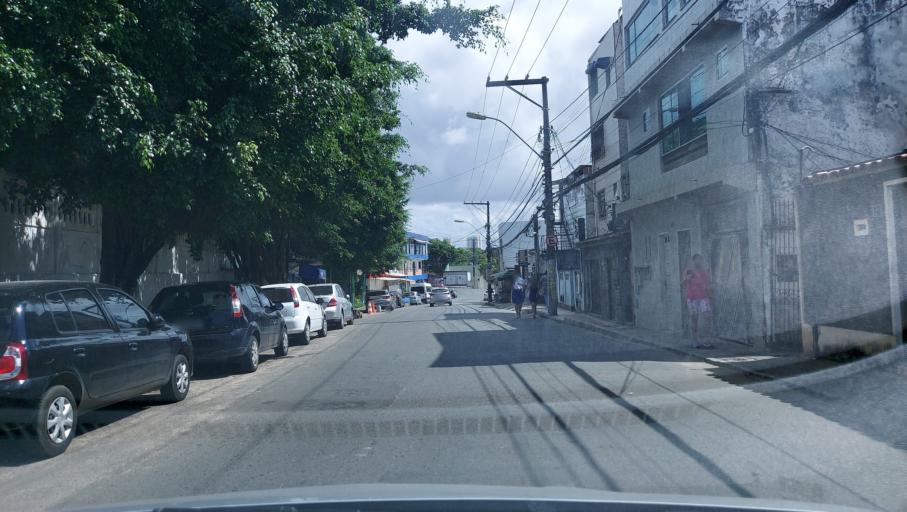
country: BR
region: Bahia
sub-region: Salvador
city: Salvador
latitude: -12.9866
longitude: -38.4775
